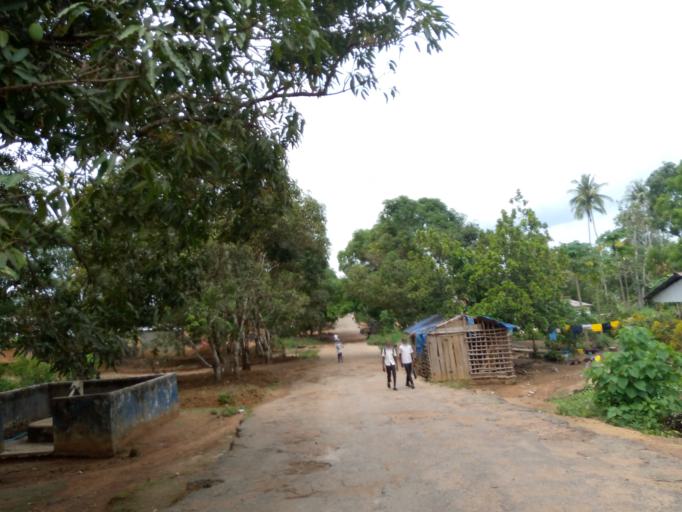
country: SL
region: Western Area
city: Waterloo
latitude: 8.3348
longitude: -13.0067
